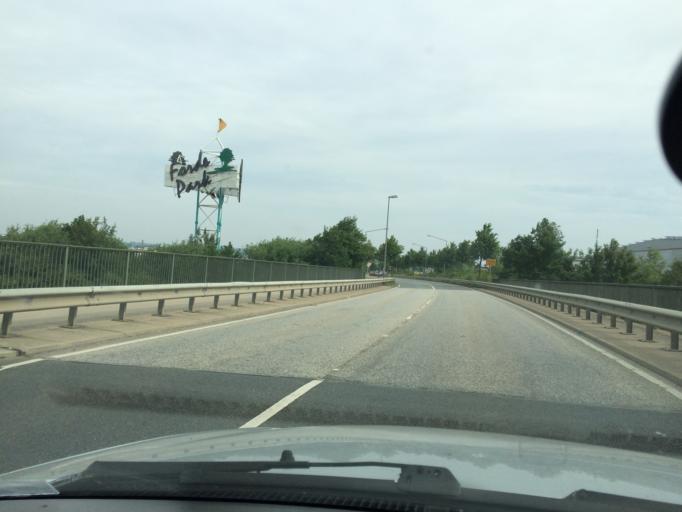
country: DE
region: Schleswig-Holstein
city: Jarplund-Weding
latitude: 54.7568
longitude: 9.4364
